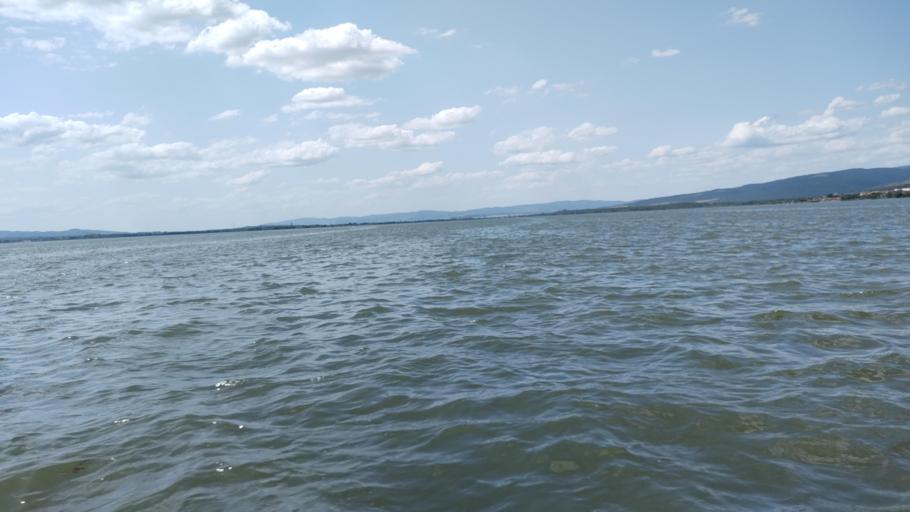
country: RO
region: Caras-Severin
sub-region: Comuna Pescari
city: Coronini
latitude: 44.6716
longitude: 21.6770
